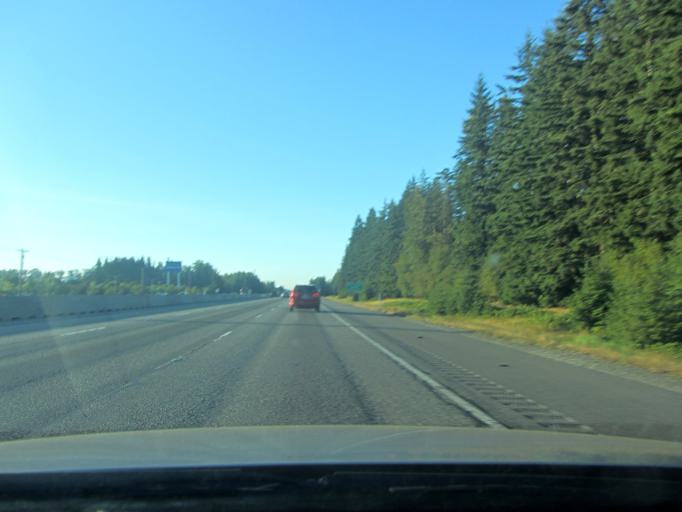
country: US
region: Washington
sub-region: Snohomish County
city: Marysville
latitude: 48.0906
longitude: -122.1846
